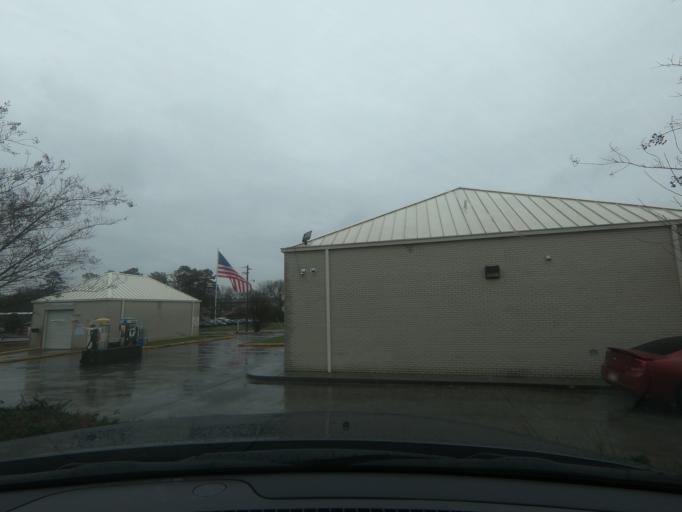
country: US
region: Georgia
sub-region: Gordon County
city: Calhoun
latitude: 34.5125
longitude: -84.9247
